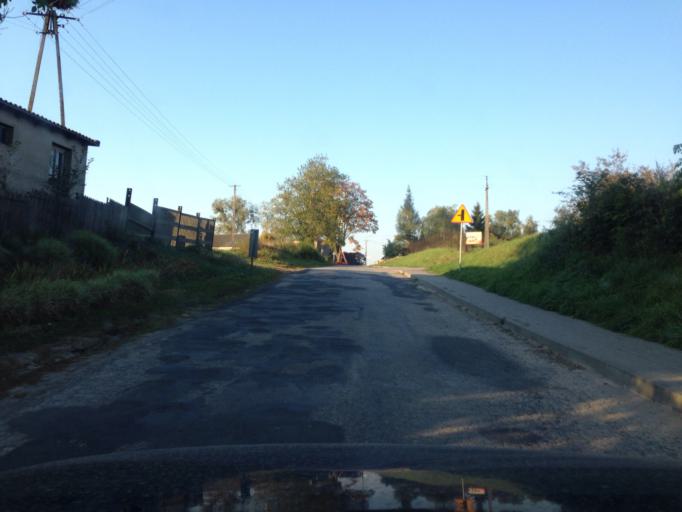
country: PL
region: Kujawsko-Pomorskie
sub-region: Powiat brodnicki
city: Gorzno
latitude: 53.2474
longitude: 19.6673
